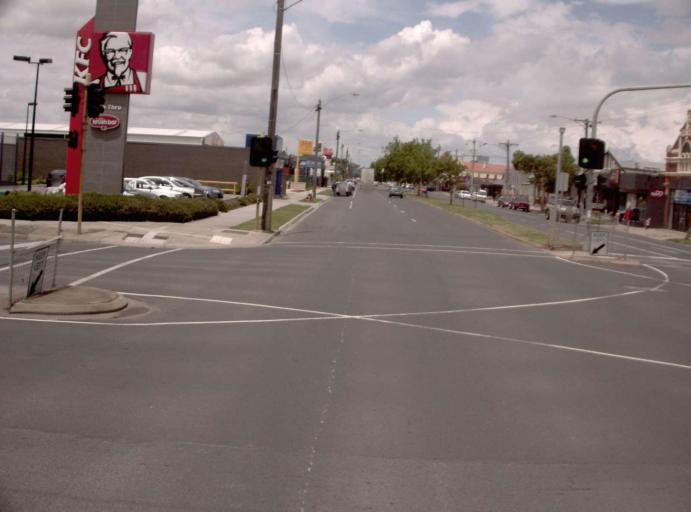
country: AU
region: Victoria
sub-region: Wellington
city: Sale
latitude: -38.1050
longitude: 147.0682
